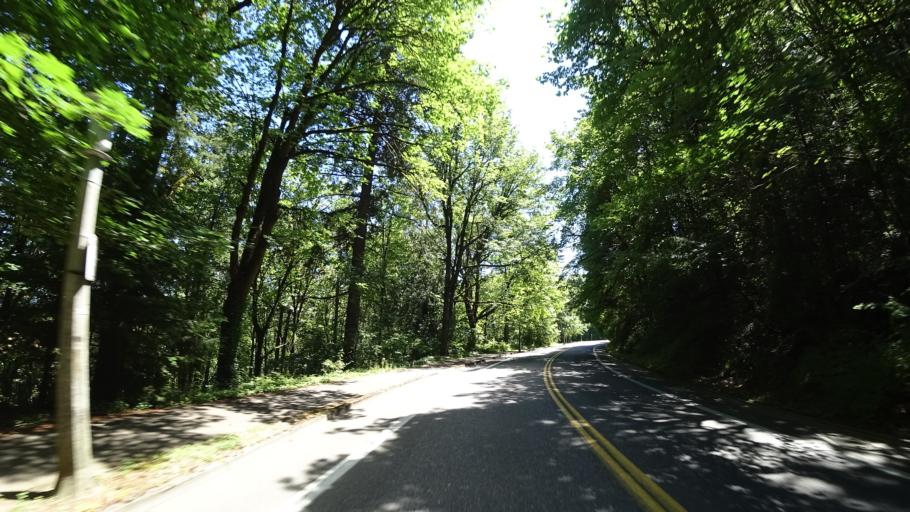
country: US
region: Oregon
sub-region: Multnomah County
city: Portland
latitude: 45.4888
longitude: -122.6851
